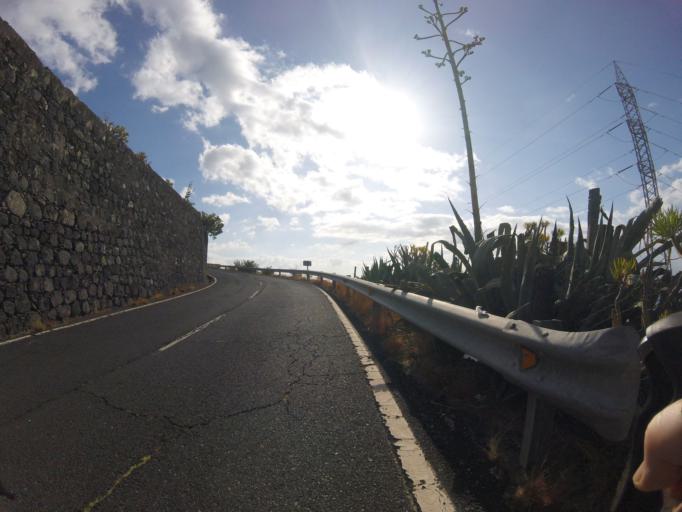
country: ES
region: Canary Islands
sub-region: Provincia de Santa Cruz de Tenerife
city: Candelaria
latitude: 28.3853
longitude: -16.3565
